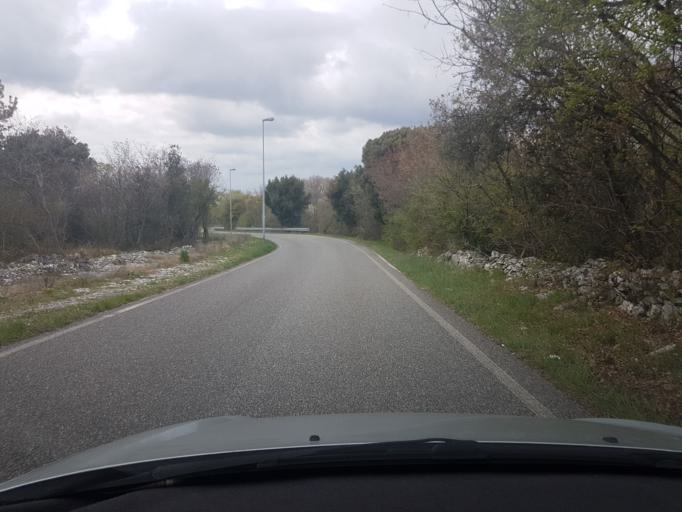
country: IT
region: Friuli Venezia Giulia
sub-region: Provincia di Trieste
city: Duino
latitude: 45.7802
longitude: 13.5963
